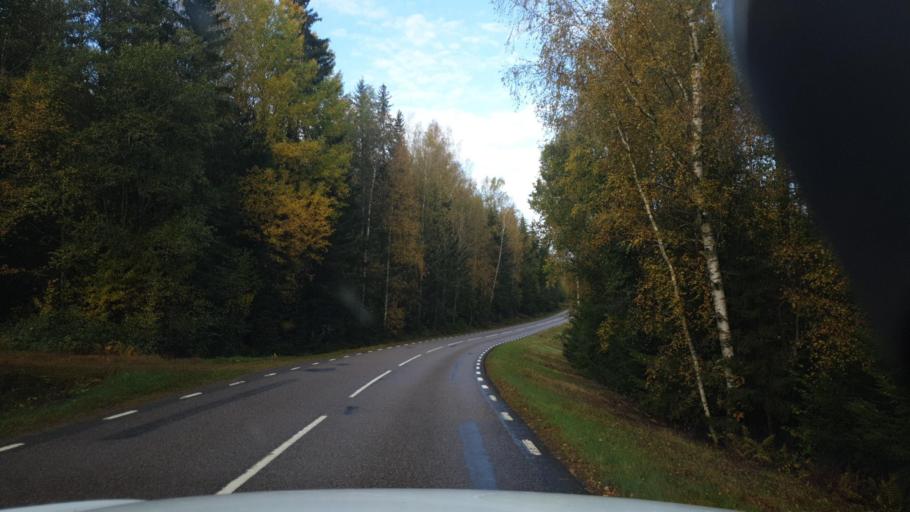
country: SE
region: Vaermland
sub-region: Arvika Kommun
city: Arvika
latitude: 59.4649
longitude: 12.7420
